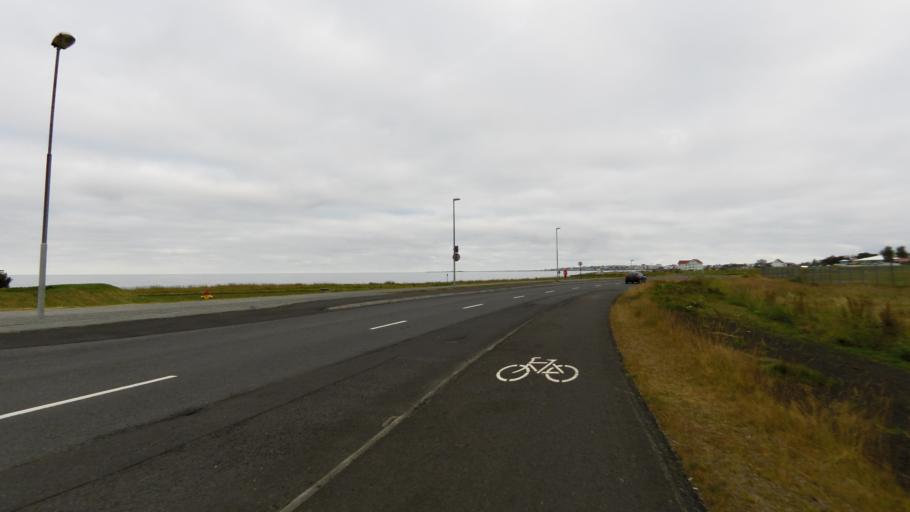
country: IS
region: Capital Region
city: Seltjarnarnes
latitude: 64.1320
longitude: -21.9580
